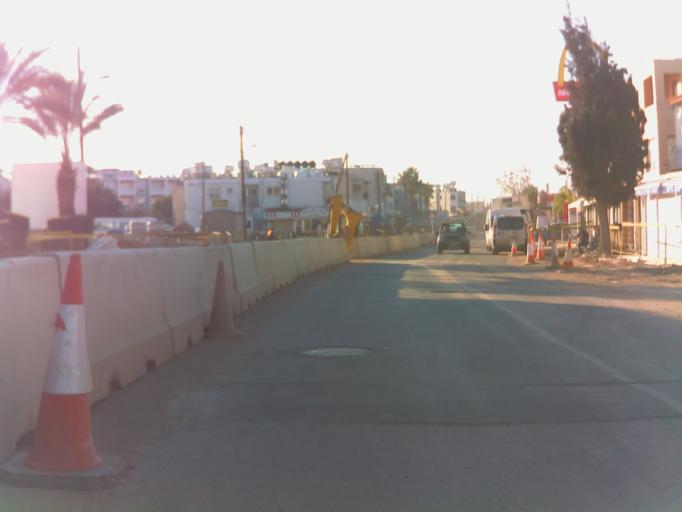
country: CY
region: Pafos
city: Paphos
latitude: 34.7708
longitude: 32.4104
